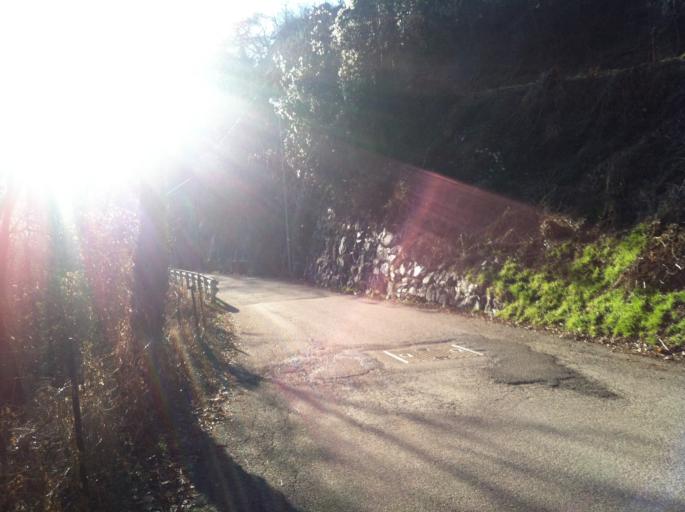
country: IT
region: Trentino-Alto Adige
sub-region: Bolzano
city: Bressanone
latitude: 46.7190
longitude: 11.6668
